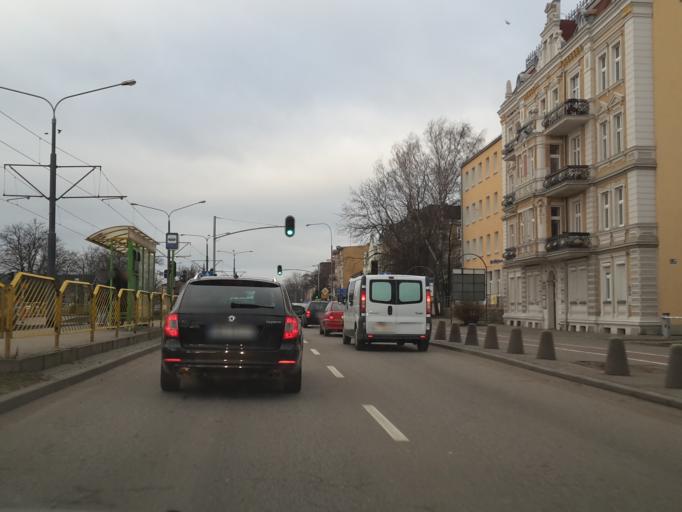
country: PL
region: Warmian-Masurian Voivodeship
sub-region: Powiat elblaski
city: Elblag
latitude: 54.1525
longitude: 19.4171
